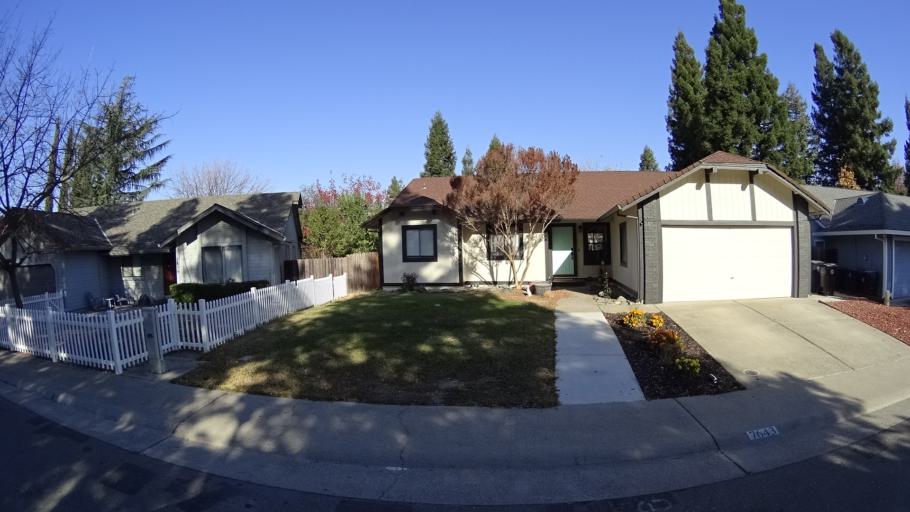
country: US
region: California
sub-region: Sacramento County
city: Citrus Heights
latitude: 38.6859
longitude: -121.2823
